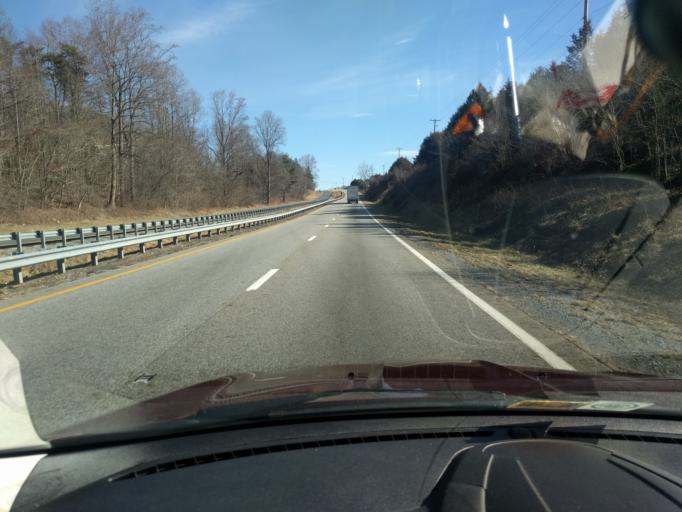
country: US
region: Virginia
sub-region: City of Bedford
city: Bedford
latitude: 37.3509
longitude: -79.6403
